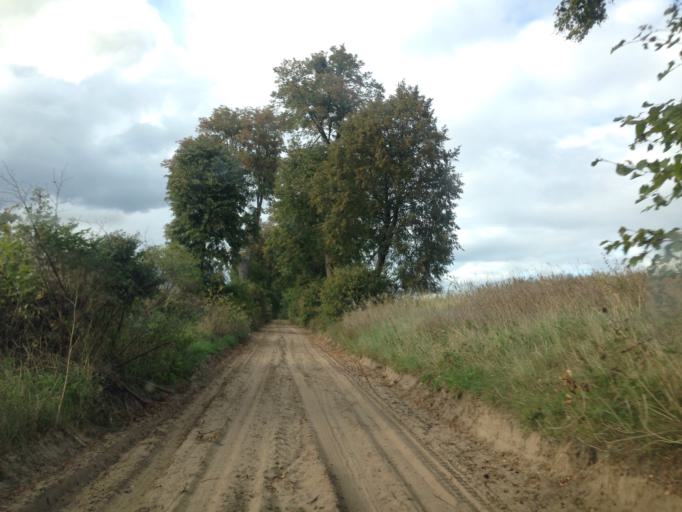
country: PL
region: Warmian-Masurian Voivodeship
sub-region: Powiat ilawski
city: Susz
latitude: 53.7467
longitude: 19.3111
